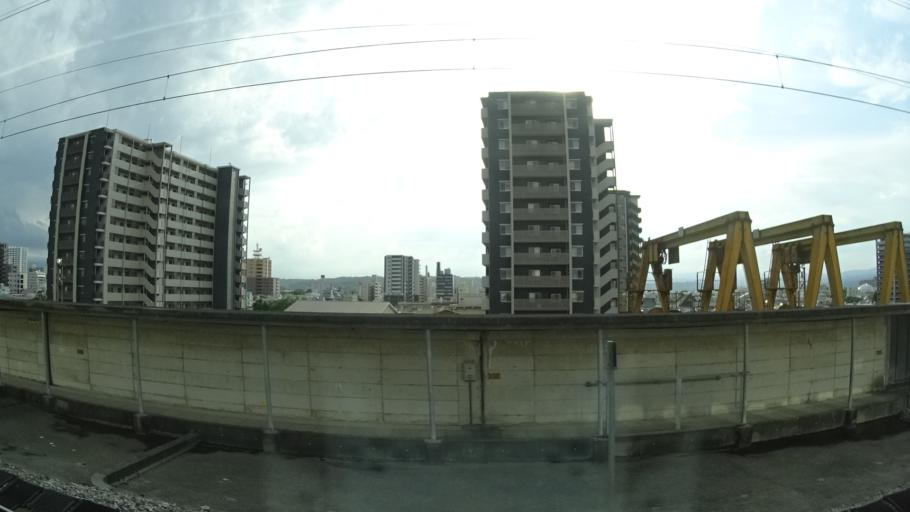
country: JP
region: Gunma
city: Takasaki
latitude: 36.3308
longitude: 139.0120
